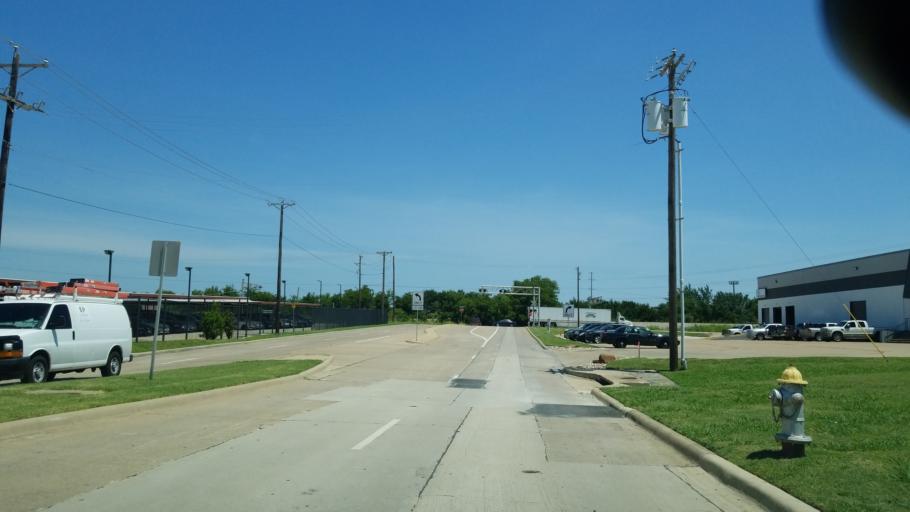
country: US
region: Texas
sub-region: Dallas County
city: Carrollton
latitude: 32.9511
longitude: -96.9161
